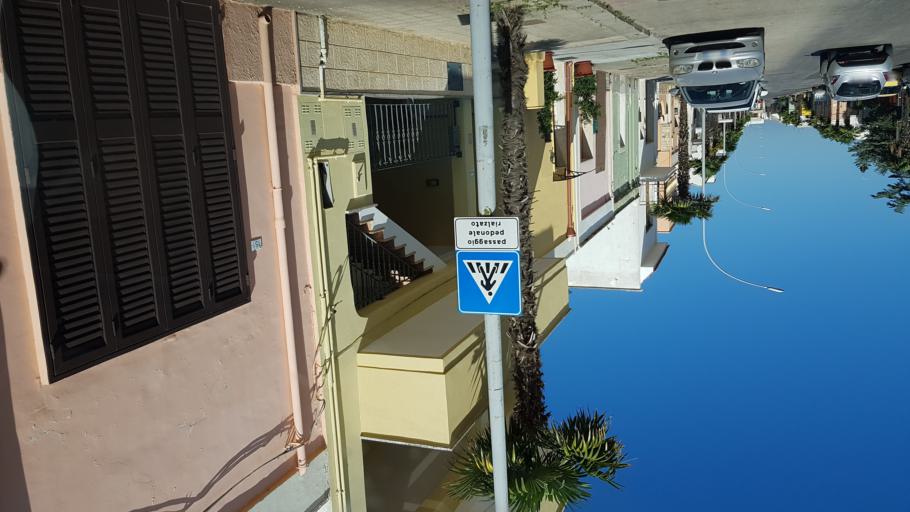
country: IT
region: Apulia
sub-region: Provincia di Brindisi
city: San Donaci
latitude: 40.4451
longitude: 17.9159
